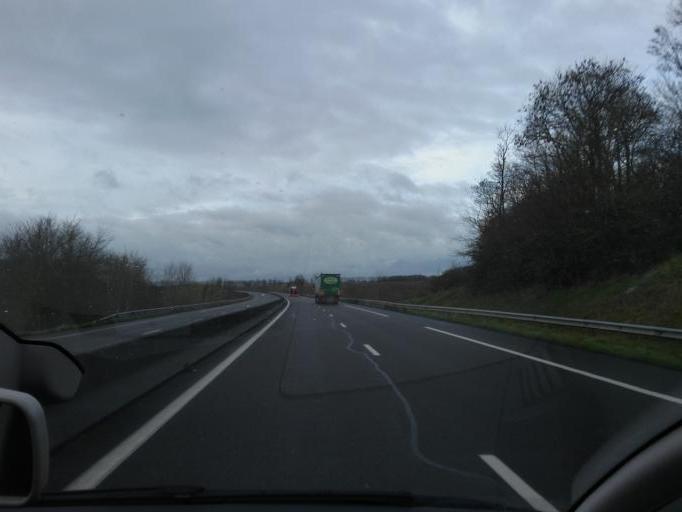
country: FR
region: Picardie
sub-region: Departement de la Somme
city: Harbonnieres
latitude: 49.8615
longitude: 2.6719
